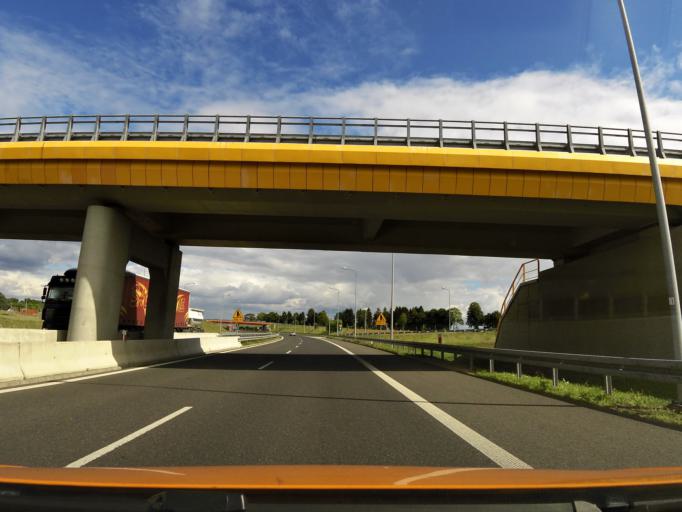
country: PL
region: West Pomeranian Voivodeship
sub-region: Powiat goleniowski
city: Nowogard
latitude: 53.6902
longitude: 15.1366
